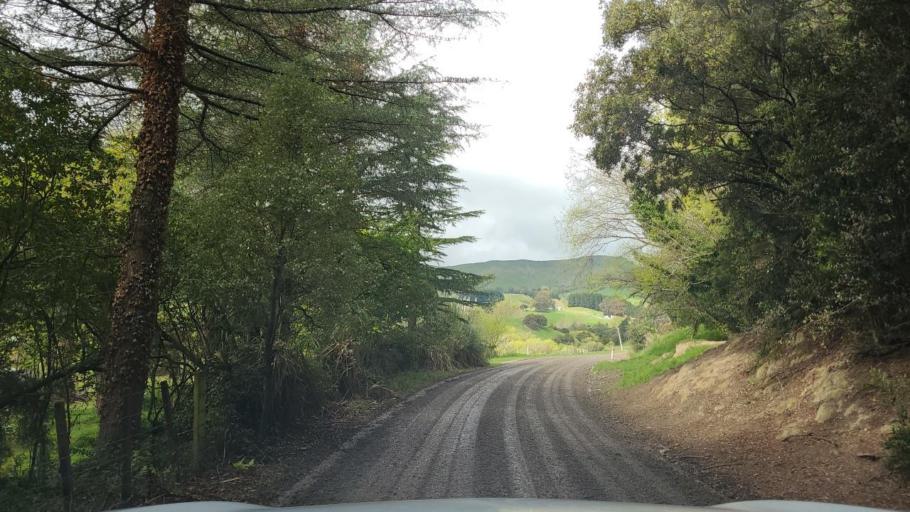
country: NZ
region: Wellington
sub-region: Masterton District
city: Masterton
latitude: -41.1701
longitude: 175.6235
